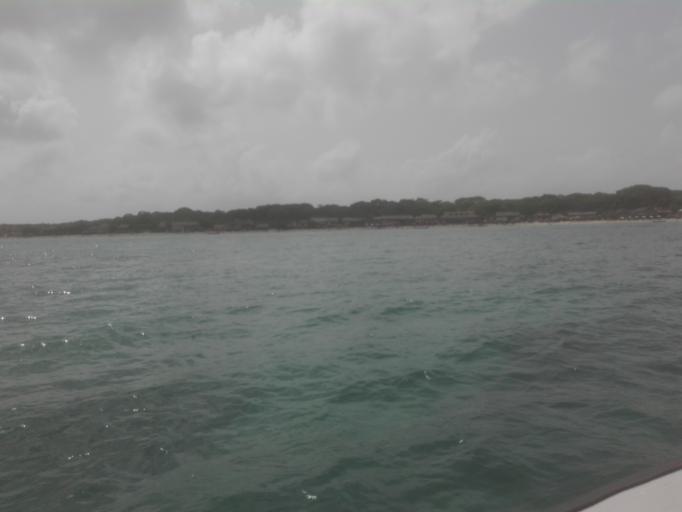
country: CO
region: Bolivar
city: Turbana
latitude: 10.2263
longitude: -75.6102
